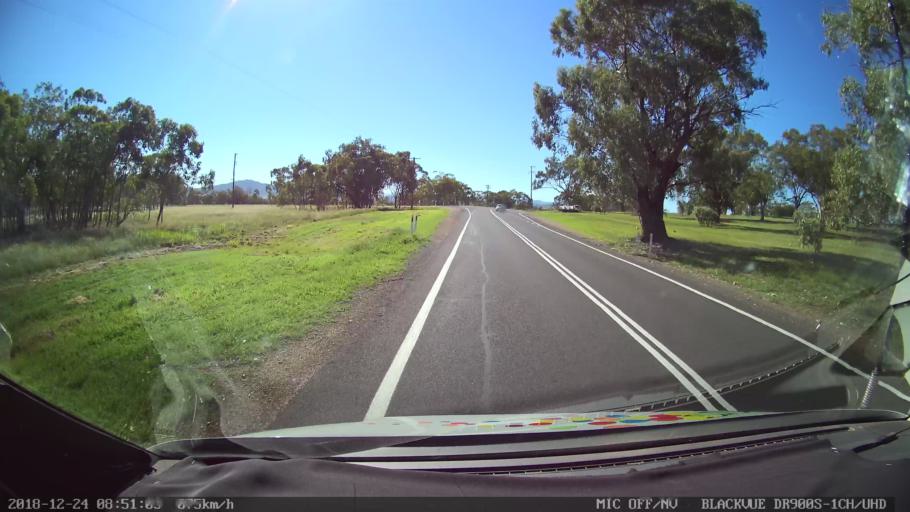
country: AU
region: New South Wales
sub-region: Liverpool Plains
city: Quirindi
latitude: -31.4812
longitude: 150.6710
